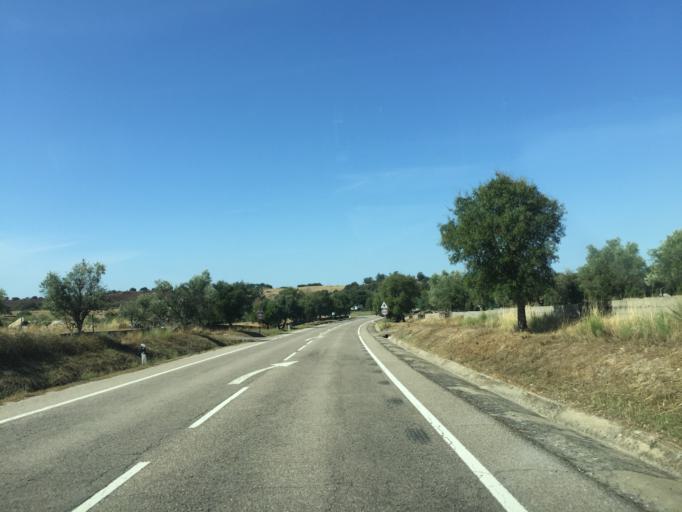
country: PT
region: Portalegre
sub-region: Castelo de Vide
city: Castelo de Vide
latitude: 39.4283
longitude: -7.4918
